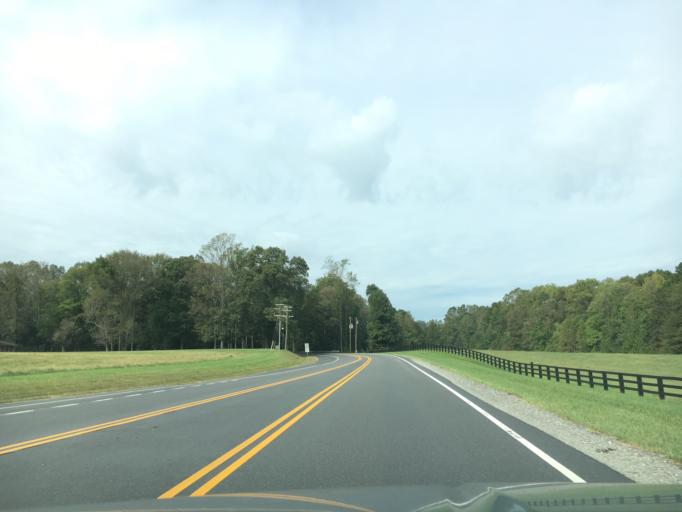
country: US
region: Virginia
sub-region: Goochland County
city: Goochland
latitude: 37.6993
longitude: -77.8325
